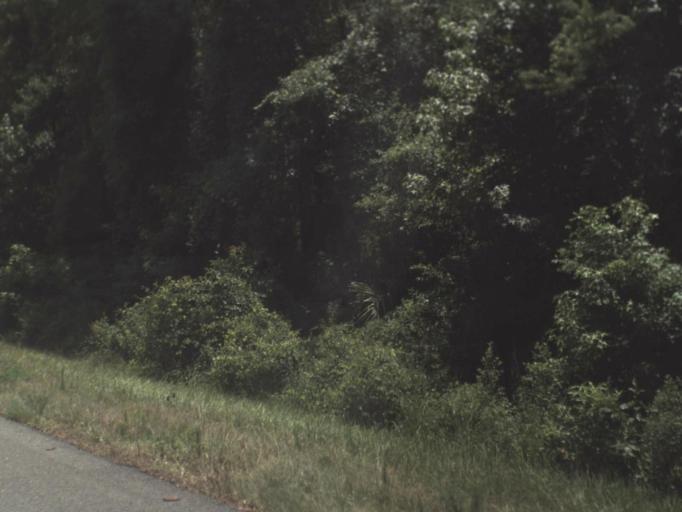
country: US
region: Florida
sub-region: Taylor County
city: Perry
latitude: 30.1183
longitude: -83.7285
